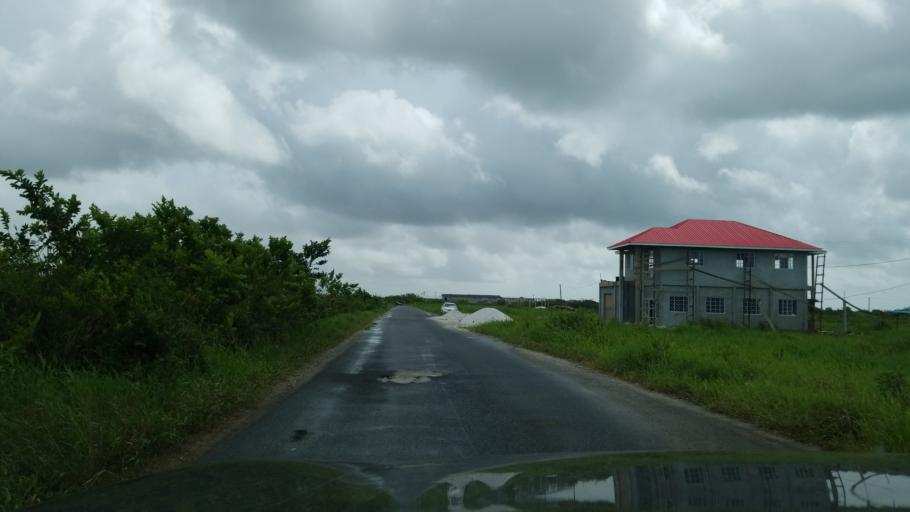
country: GY
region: Demerara-Mahaica
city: Georgetown
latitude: 6.7547
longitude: -58.1621
